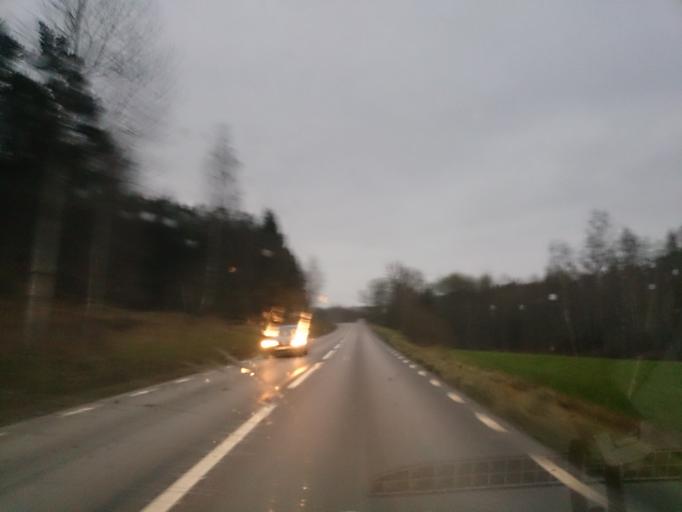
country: SE
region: OEstergoetland
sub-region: Atvidabergs Kommun
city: Atvidaberg
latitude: 58.2822
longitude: 15.9026
